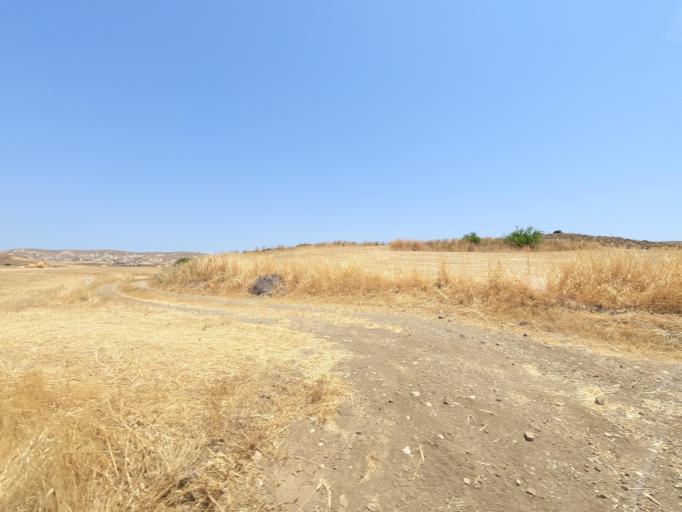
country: CY
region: Larnaka
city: Troulloi
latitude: 35.0203
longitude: 33.6377
